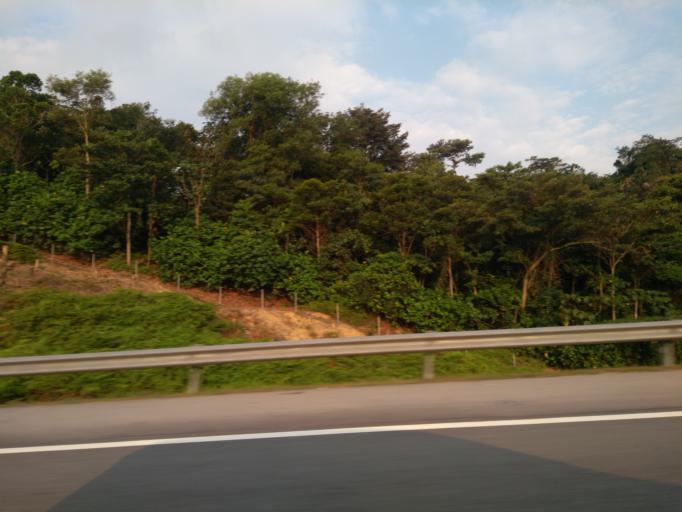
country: MY
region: Putrajaya
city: Putrajaya
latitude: 2.9823
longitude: 101.6830
